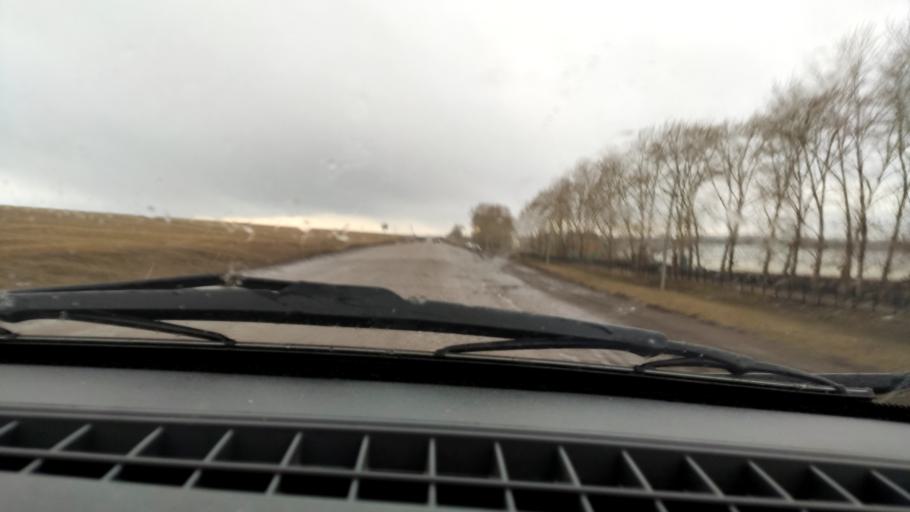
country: RU
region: Bashkortostan
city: Chekmagush
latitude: 55.1182
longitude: 54.8073
